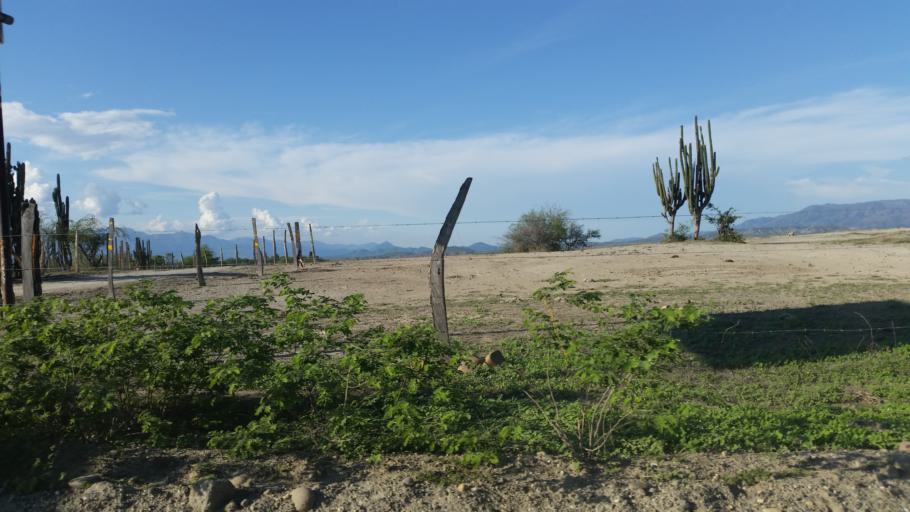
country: CO
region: Huila
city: Villavieja
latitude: 3.2323
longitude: -75.1553
